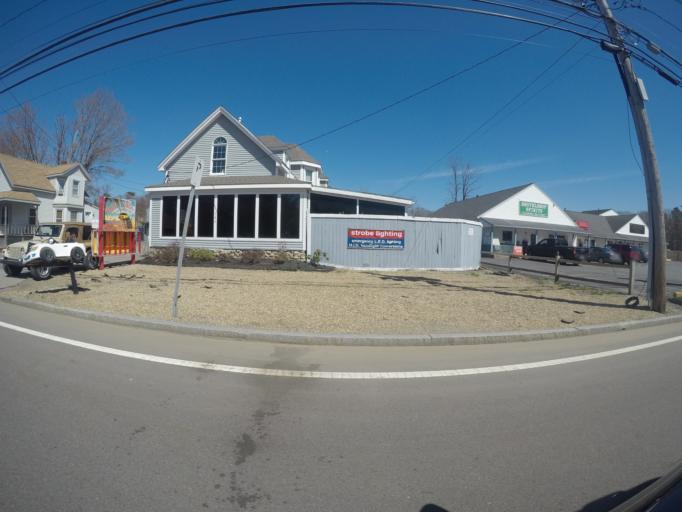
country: US
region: Massachusetts
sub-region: Norfolk County
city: Stoughton
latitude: 42.0679
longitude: -71.0873
